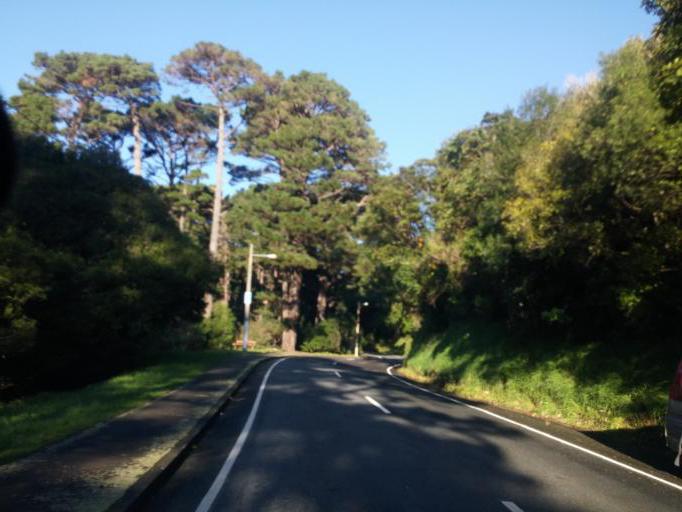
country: NZ
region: Wellington
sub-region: Wellington City
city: Wellington
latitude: -41.2993
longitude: 174.7664
